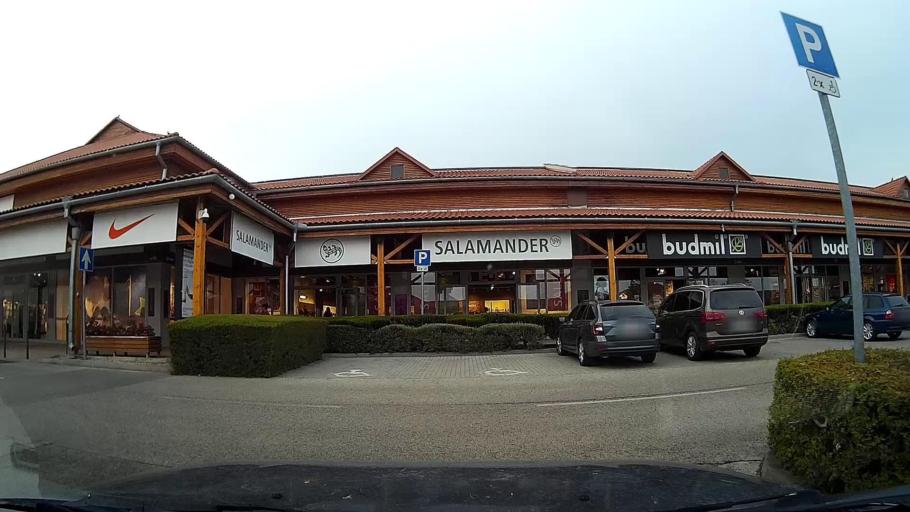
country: HU
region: Pest
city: Toeroekbalint
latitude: 47.4657
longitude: 18.8882
